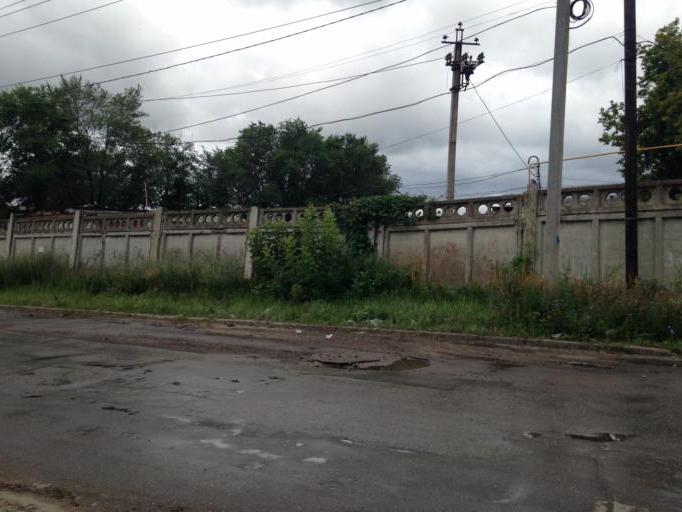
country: RU
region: Ulyanovsk
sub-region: Ulyanovskiy Rayon
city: Ulyanovsk
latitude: 54.2456
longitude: 48.3063
